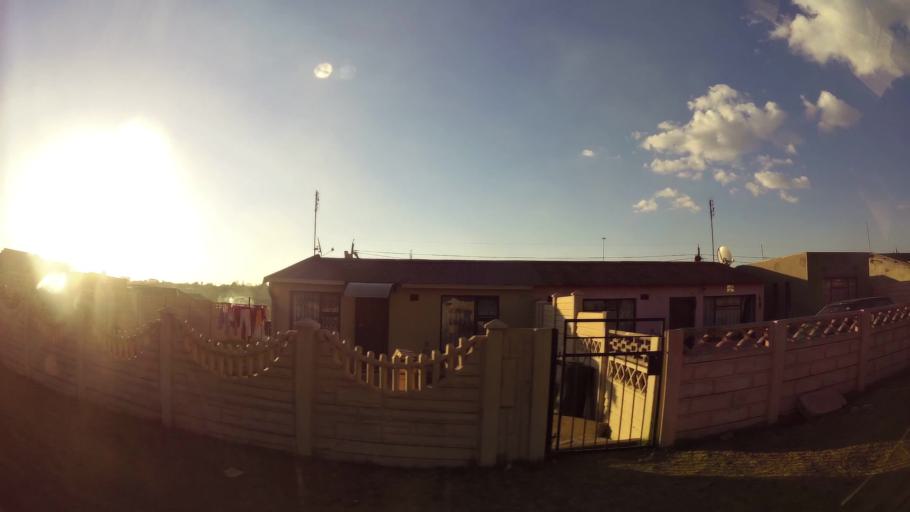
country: ZA
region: Mpumalanga
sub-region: Nkangala District Municipality
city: Witbank
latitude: -25.8766
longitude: 29.1891
